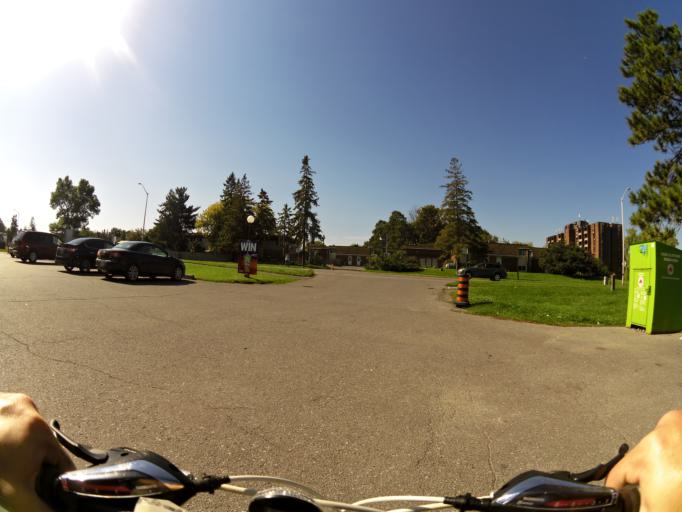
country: CA
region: Ontario
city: Bells Corners
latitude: 45.3306
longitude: -75.9006
